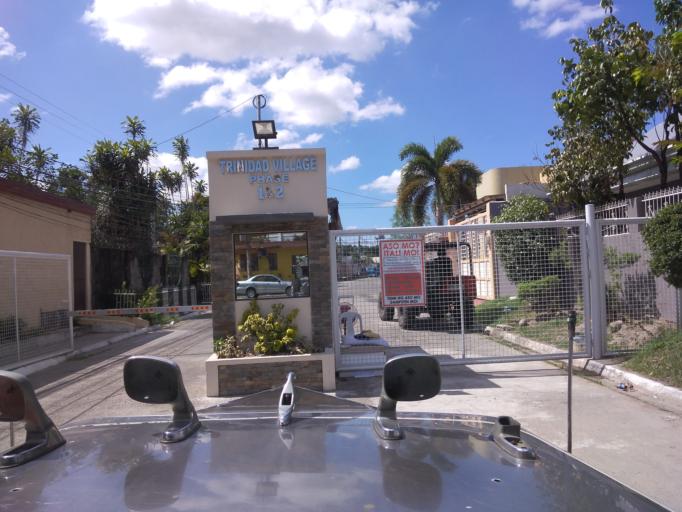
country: PH
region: Central Luzon
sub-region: Province of Pampanga
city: Calibutbut
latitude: 15.1190
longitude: 120.6010
